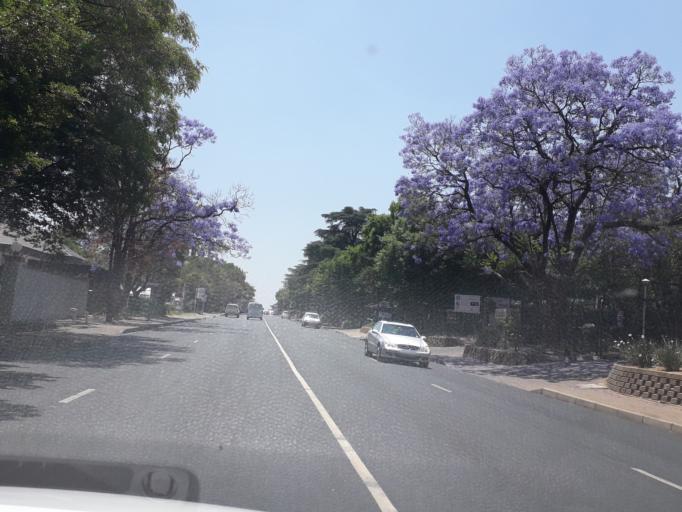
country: ZA
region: Gauteng
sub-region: City of Johannesburg Metropolitan Municipality
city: Johannesburg
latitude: -26.0989
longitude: 27.9992
